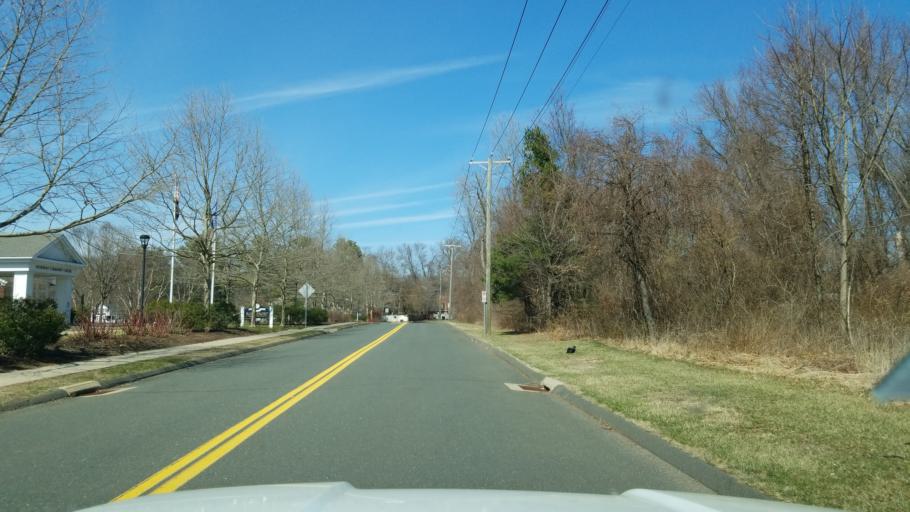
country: US
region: Connecticut
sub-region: Hartford County
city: Glastonbury
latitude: 41.7138
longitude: -72.6169
